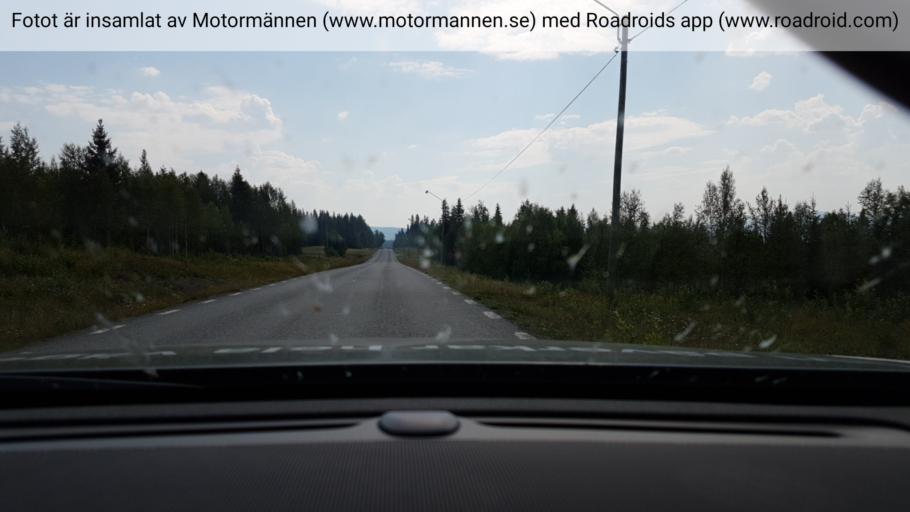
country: SE
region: Vaesterbotten
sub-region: Vilhelmina Kommun
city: Sjoberg
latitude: 65.4659
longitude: 16.0758
